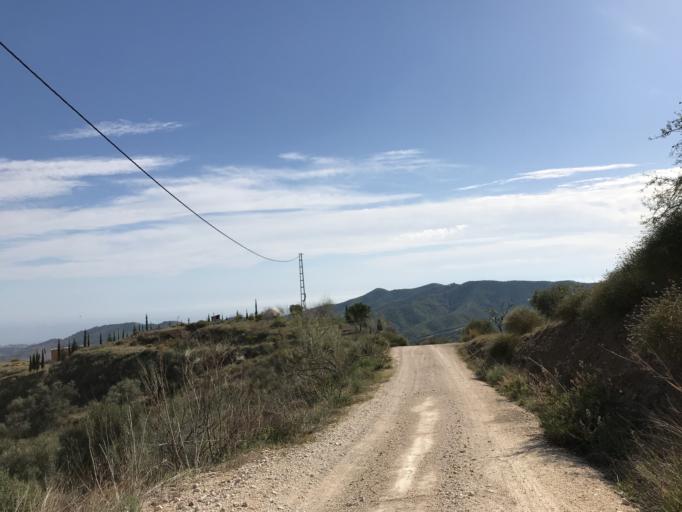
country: ES
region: Andalusia
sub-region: Provincia de Malaga
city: Valdes
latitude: 36.7758
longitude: -4.2176
